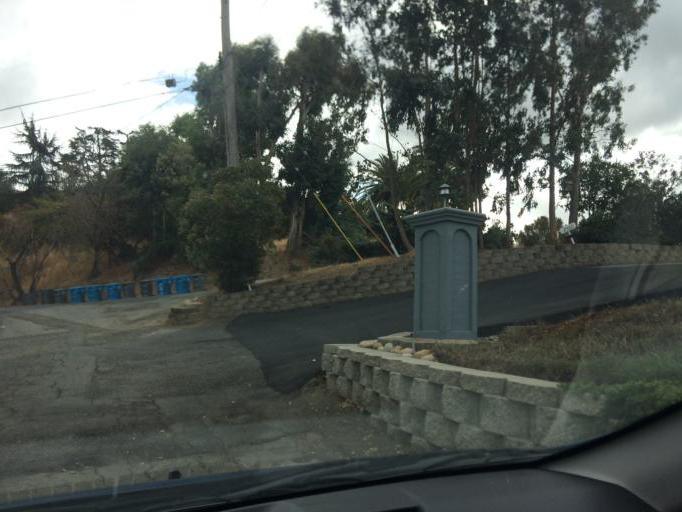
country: US
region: California
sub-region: Santa Clara County
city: Alum Rock
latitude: 37.3401
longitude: -121.7775
